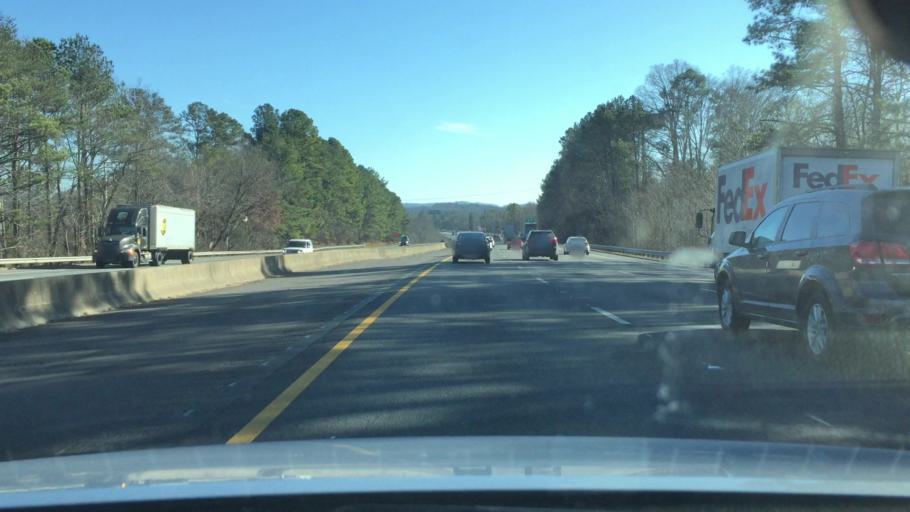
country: US
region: Georgia
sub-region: Catoosa County
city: Ringgold
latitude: 34.9010
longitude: -85.0864
